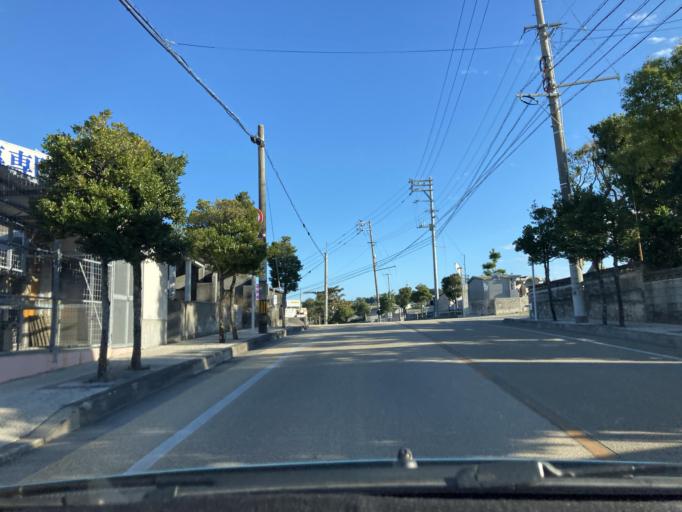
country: JP
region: Okinawa
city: Naha-shi
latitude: 26.2075
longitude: 127.7153
